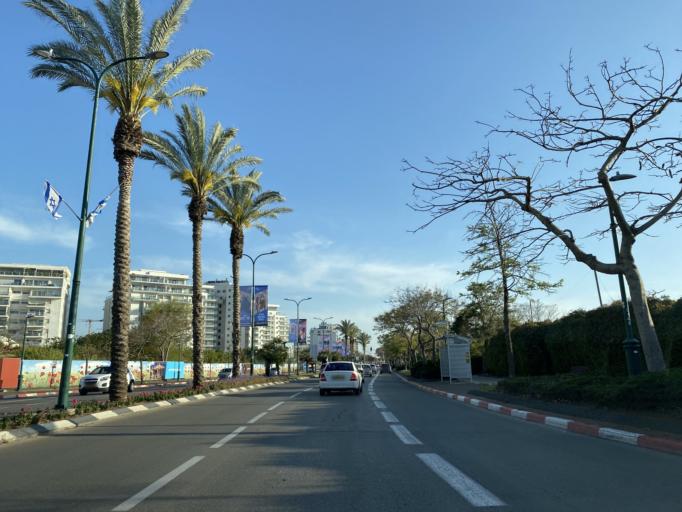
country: IL
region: Tel Aviv
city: Herzliyya
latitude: 32.1686
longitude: 34.8285
